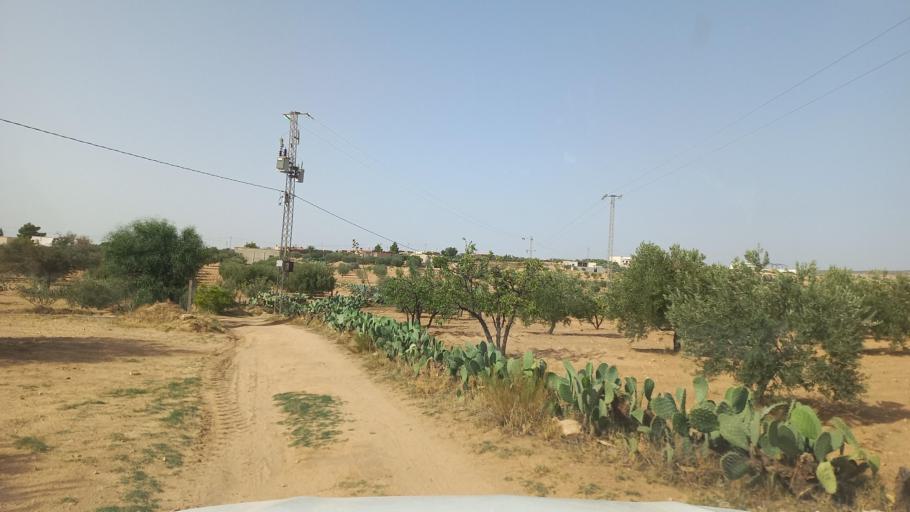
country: TN
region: Al Qasrayn
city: Kasserine
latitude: 35.2987
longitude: 8.9581
